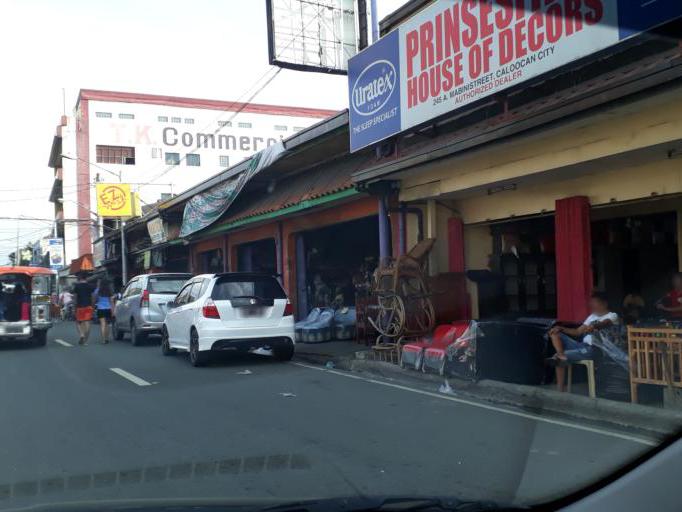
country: PH
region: Metro Manila
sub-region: Caloocan City
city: Niugan
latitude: 14.6451
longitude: 120.9747
